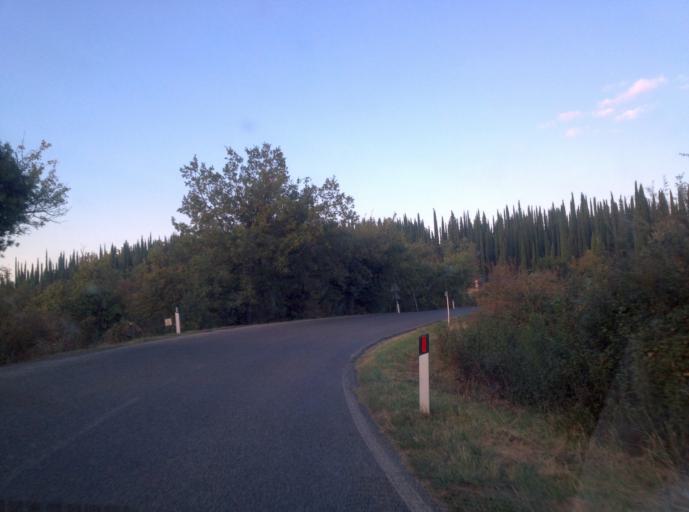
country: IT
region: Tuscany
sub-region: Provincia di Siena
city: Castellina in Chianti
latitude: 43.4415
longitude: 11.3004
